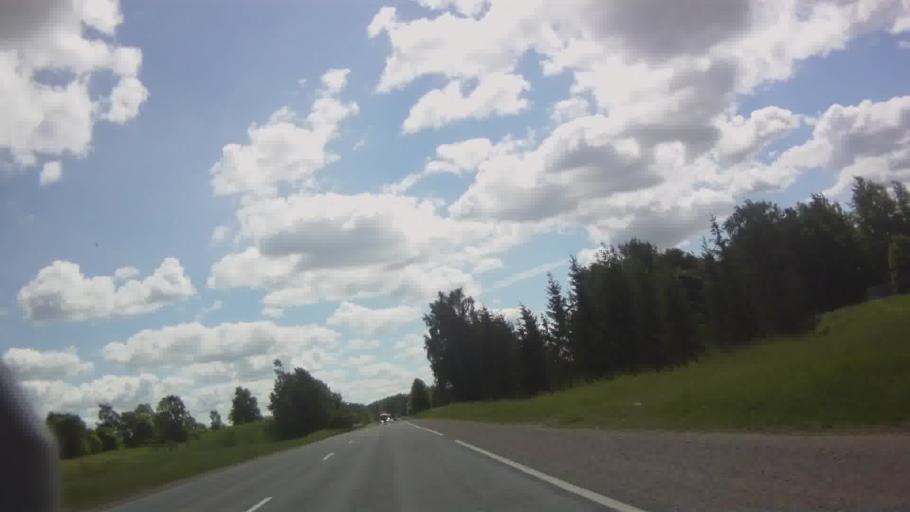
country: LV
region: Vilanu
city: Vilani
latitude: 56.5924
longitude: 26.8800
